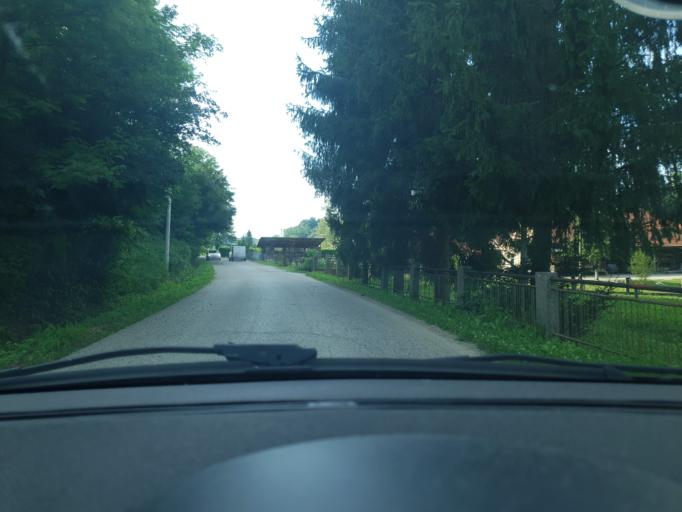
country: HR
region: Zagrebacka
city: Jakovlje
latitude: 46.0205
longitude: 15.8371
